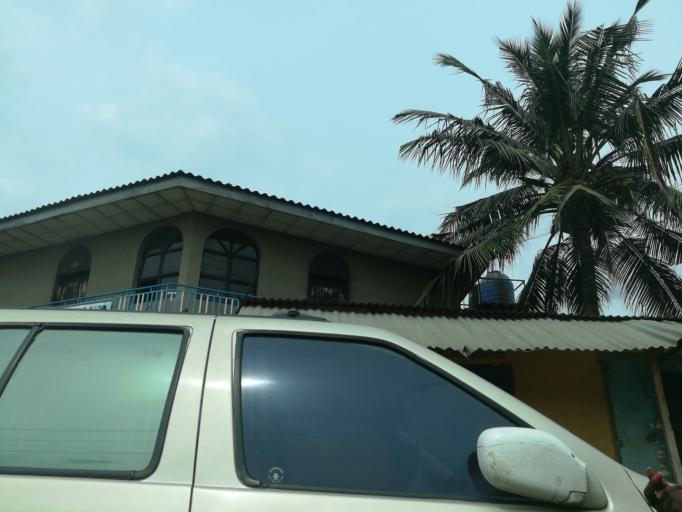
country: NG
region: Lagos
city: Ojota
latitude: 6.6100
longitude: 3.4143
